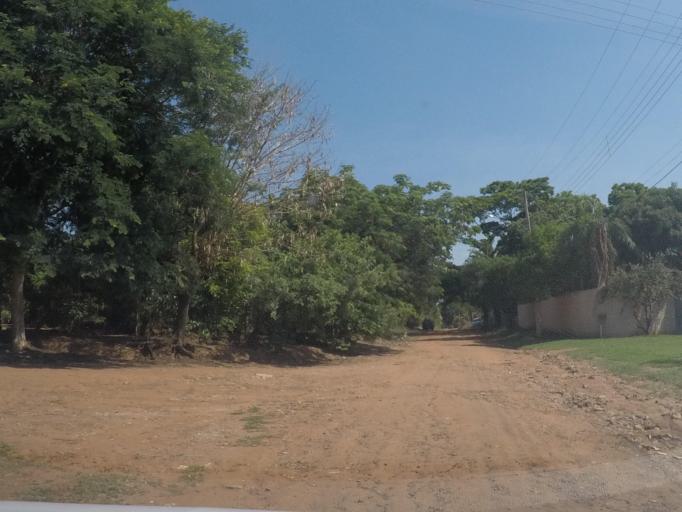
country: BR
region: Sao Paulo
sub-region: Monte Mor
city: Monte Mor
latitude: -22.8824
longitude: -47.2974
